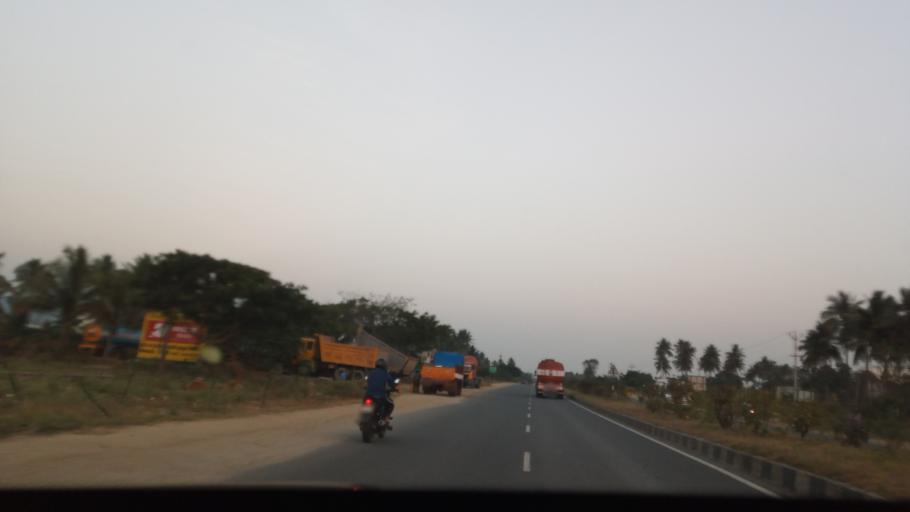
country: IN
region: Tamil Nadu
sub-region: Salem
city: Belur
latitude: 11.6651
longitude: 78.2942
